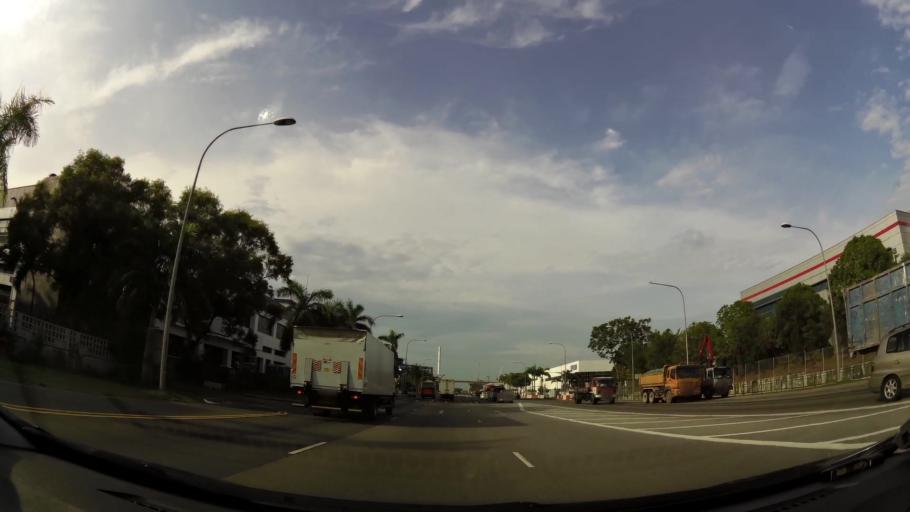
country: MY
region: Johor
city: Johor Bahru
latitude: 1.3353
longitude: 103.6433
